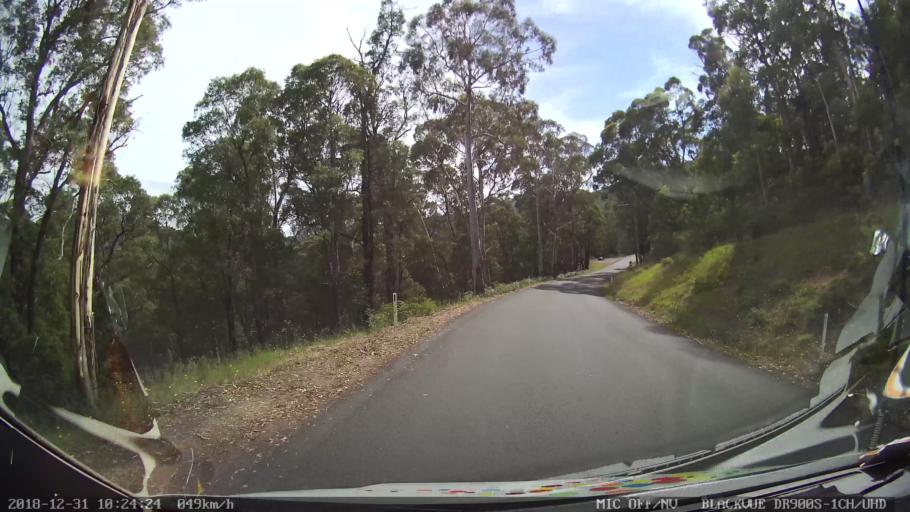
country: AU
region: New South Wales
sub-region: Snowy River
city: Jindabyne
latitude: -36.5125
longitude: 148.1398
